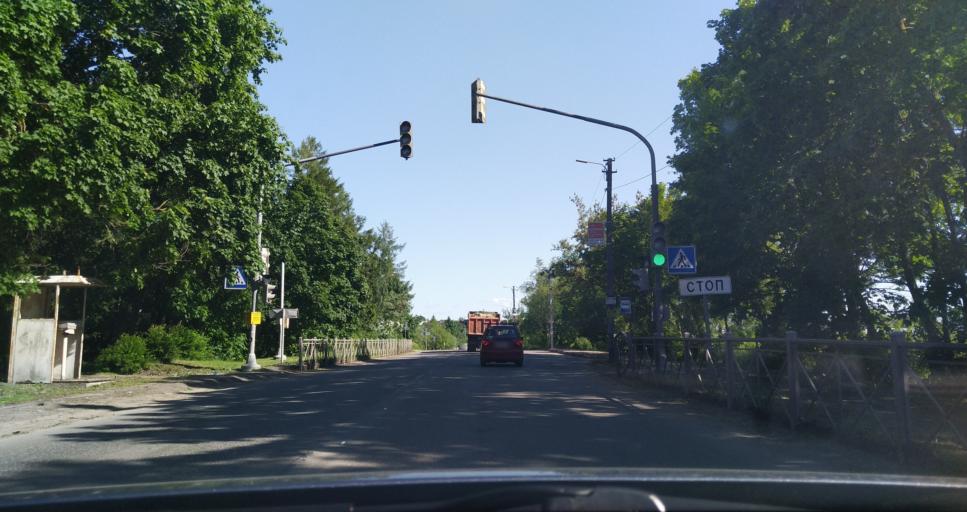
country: RU
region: Leningrad
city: Taytsy
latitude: 59.6970
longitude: 30.1041
